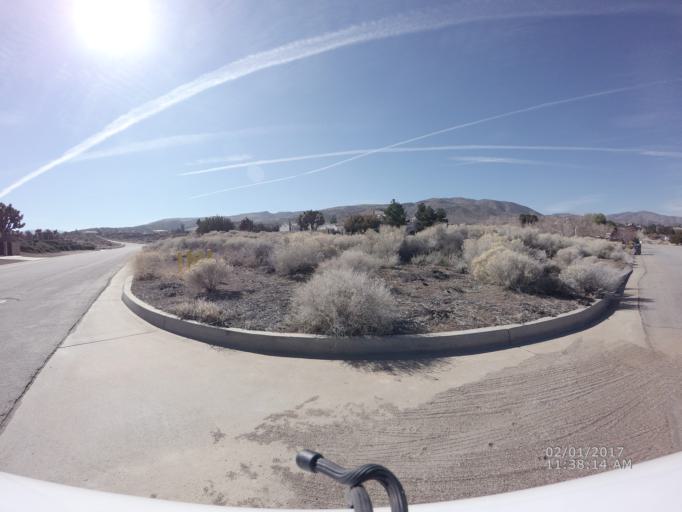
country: US
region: California
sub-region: Los Angeles County
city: Palmdale
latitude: 34.5456
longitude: -118.1166
